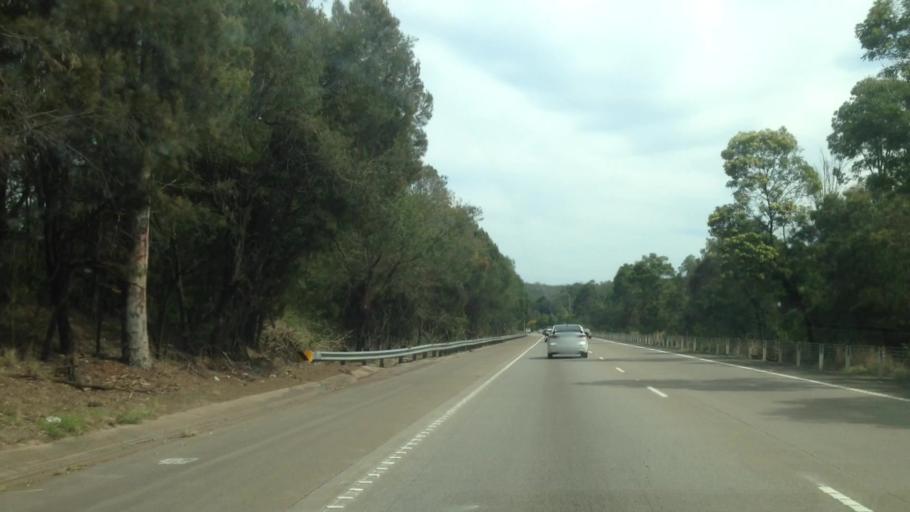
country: AU
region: New South Wales
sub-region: Lake Macquarie Shire
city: Fennell Bay
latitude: -32.9810
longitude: 151.5255
